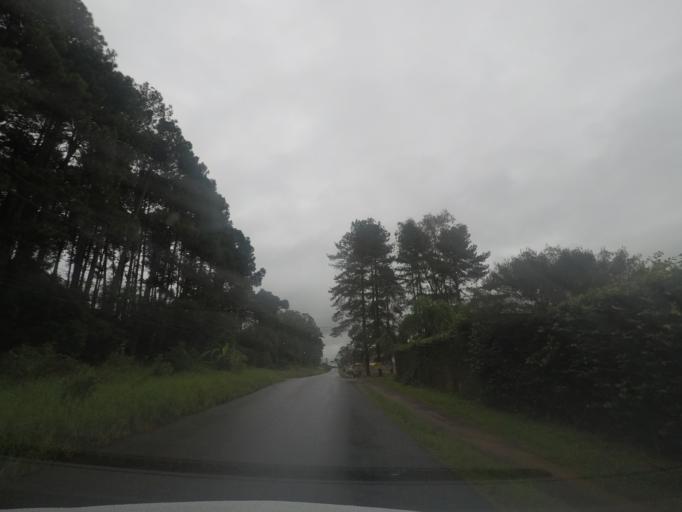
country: BR
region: Parana
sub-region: Quatro Barras
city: Quatro Barras
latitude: -25.3851
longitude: -49.1367
